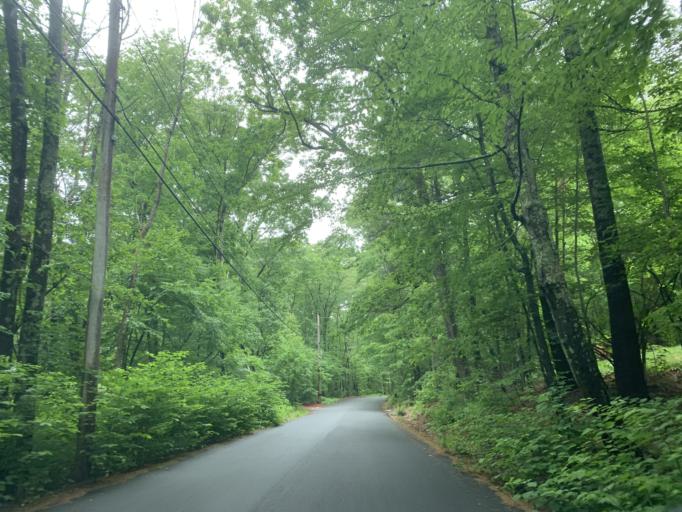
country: US
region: Massachusetts
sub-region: Worcester County
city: Upton
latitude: 42.1765
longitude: -71.6174
